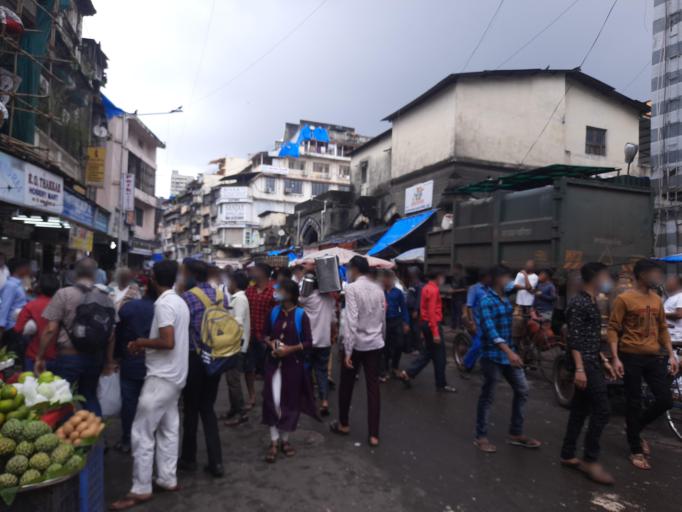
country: IN
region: Maharashtra
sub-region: Mumbai Suburban
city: Mumbai
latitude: 18.9525
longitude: 72.8297
